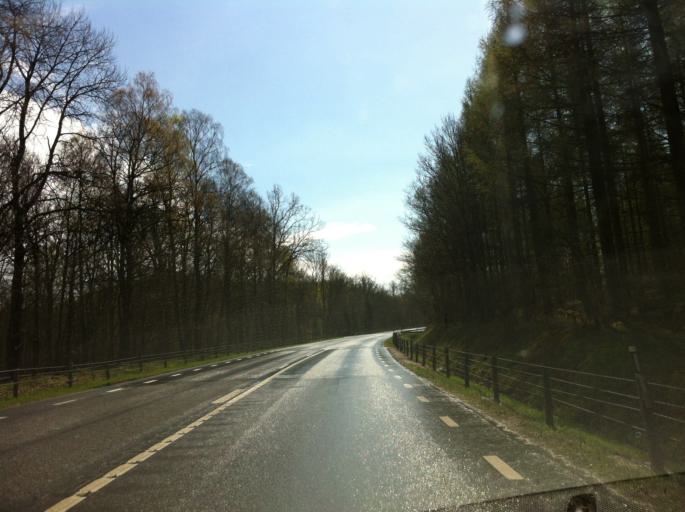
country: SE
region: Skane
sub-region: Horby Kommun
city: Hoerby
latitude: 55.8989
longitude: 13.6170
